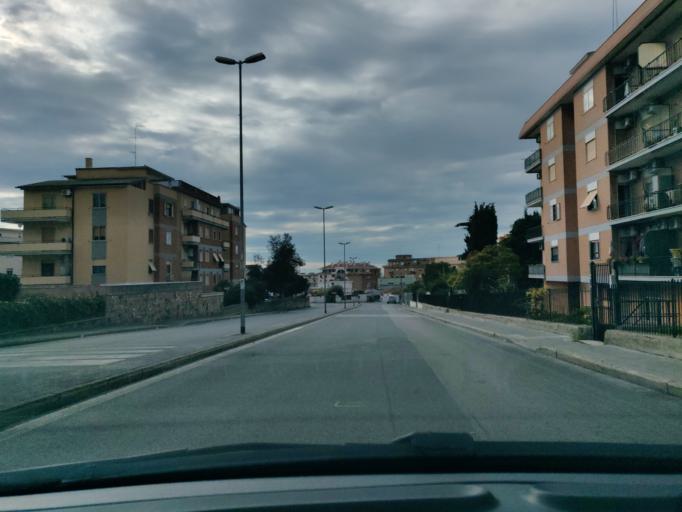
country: IT
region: Latium
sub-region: Citta metropolitana di Roma Capitale
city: Civitavecchia
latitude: 42.0935
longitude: 11.8093
